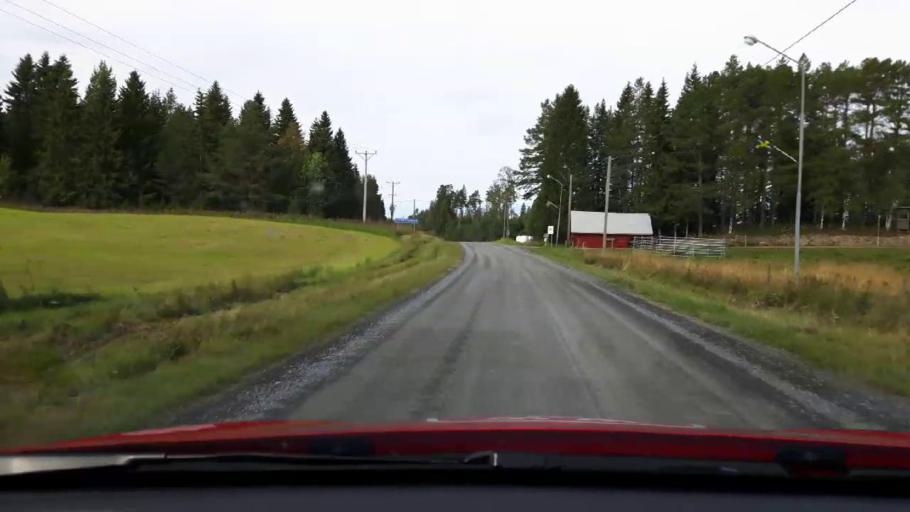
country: SE
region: Jaemtland
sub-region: Krokoms Kommun
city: Valla
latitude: 63.2556
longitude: 13.9450
